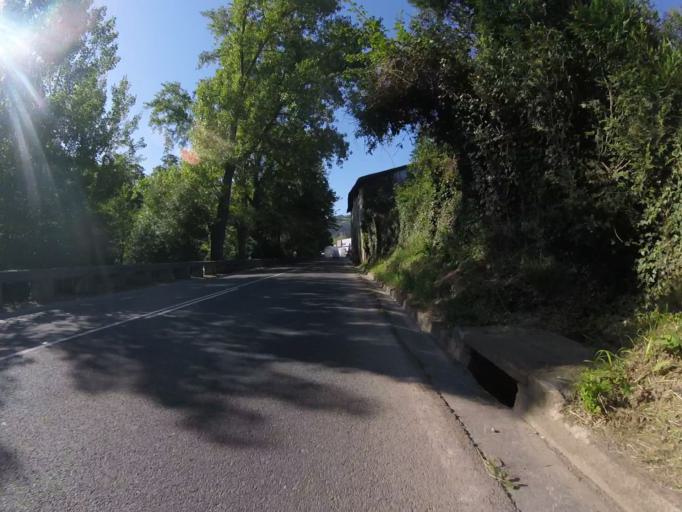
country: ES
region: Basque Country
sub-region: Provincia de Guipuzcoa
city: Azpeitia
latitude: 43.1668
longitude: -2.2493
